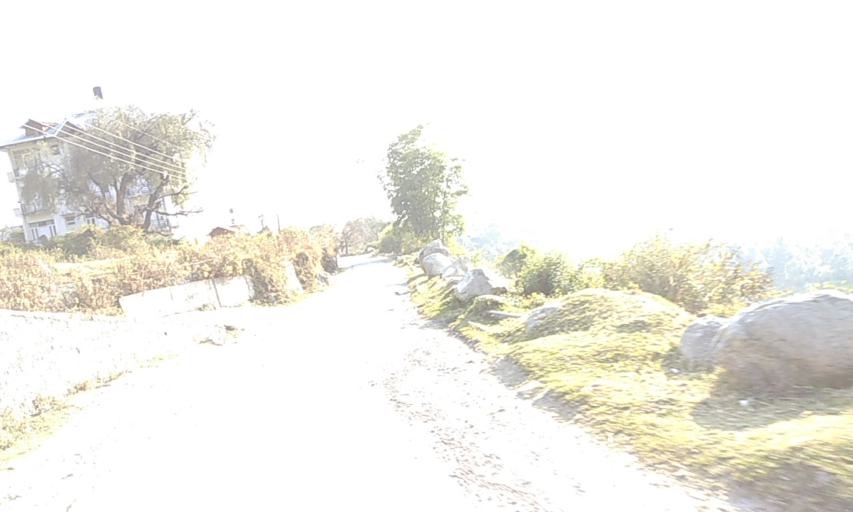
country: IN
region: Himachal Pradesh
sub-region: Kangra
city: Palampur
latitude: 32.1322
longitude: 76.5361
